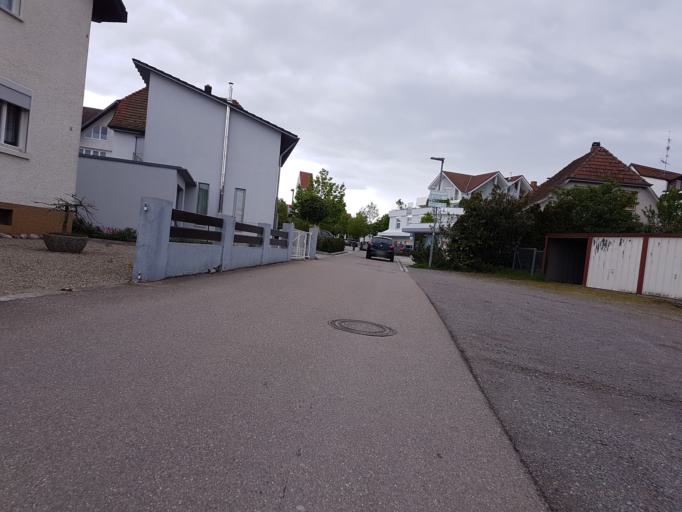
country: DE
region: Baden-Wuerttemberg
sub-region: Freiburg Region
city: Lauchringen
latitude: 47.6288
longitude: 8.3021
